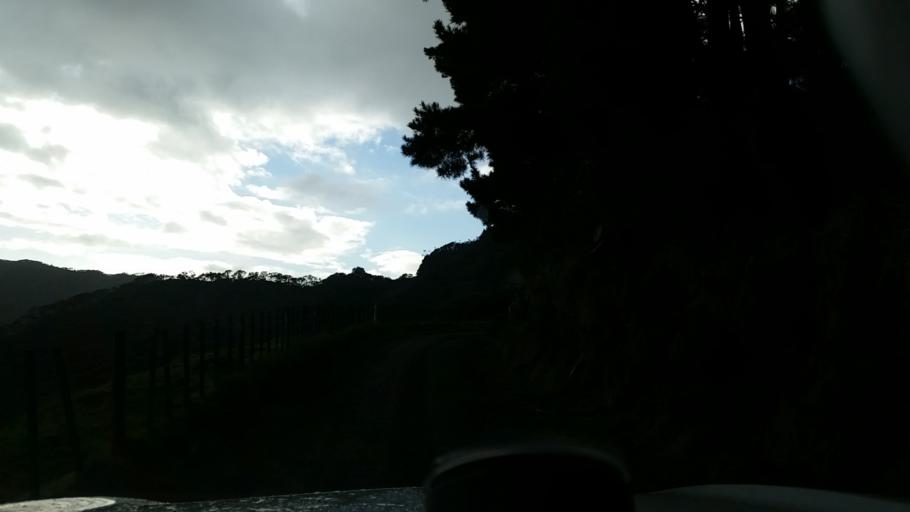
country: NZ
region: Taranaki
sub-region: South Taranaki District
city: Eltham
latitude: -39.4079
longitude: 174.5441
